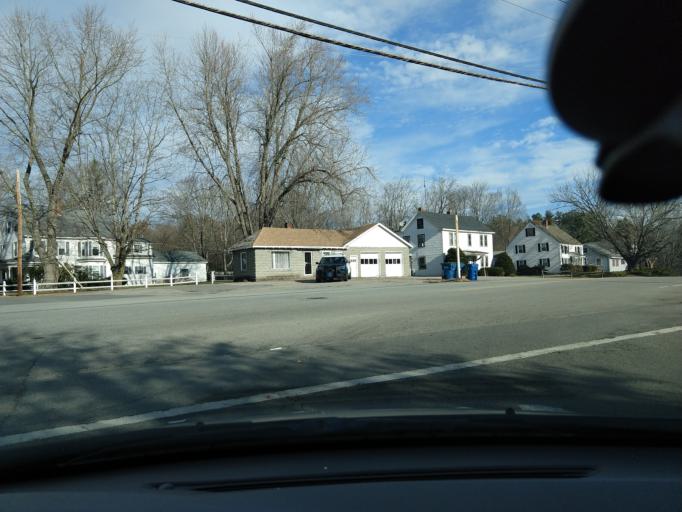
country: US
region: Massachusetts
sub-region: Middlesex County
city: East Pepperell
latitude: 42.6739
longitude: -71.5766
